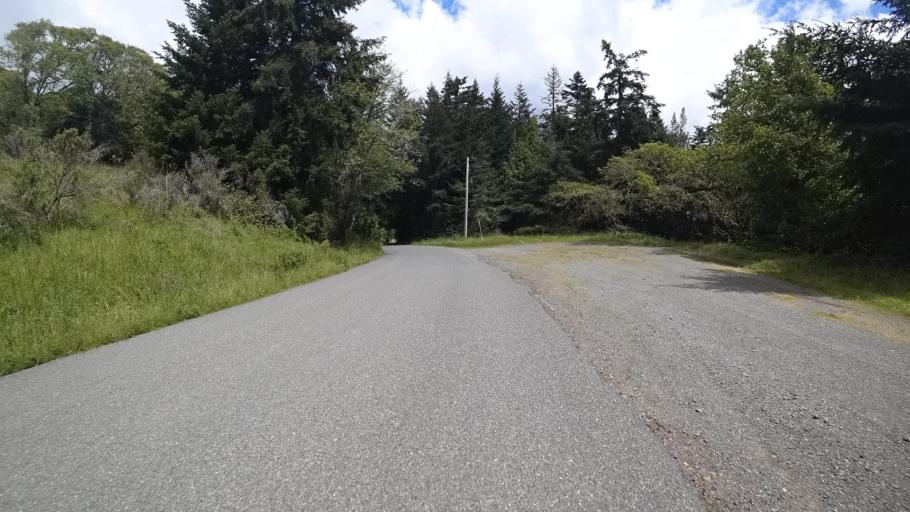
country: US
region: California
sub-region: Humboldt County
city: Blue Lake
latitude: 40.8437
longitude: -123.9082
